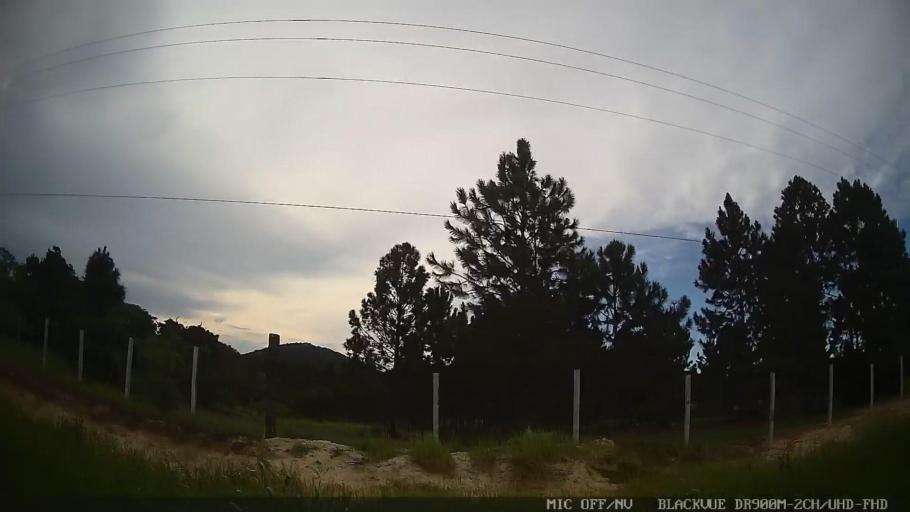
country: BR
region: Sao Paulo
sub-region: Iguape
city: Iguape
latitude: -24.6778
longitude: -47.4577
